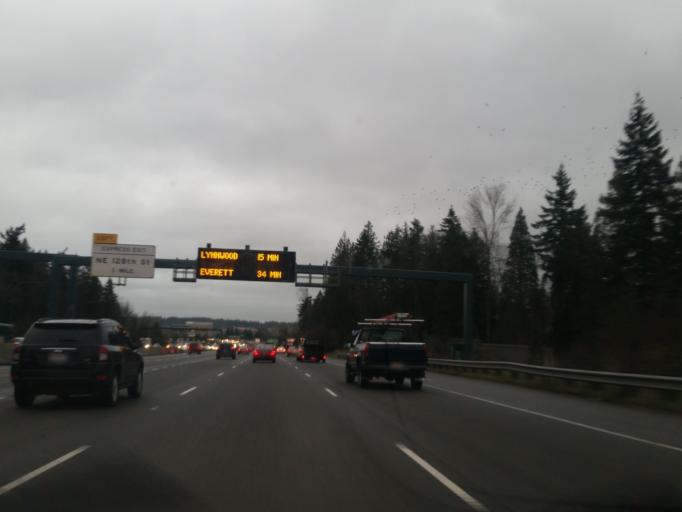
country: US
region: Washington
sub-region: King County
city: Kirkland
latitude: 47.6927
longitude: -122.1807
